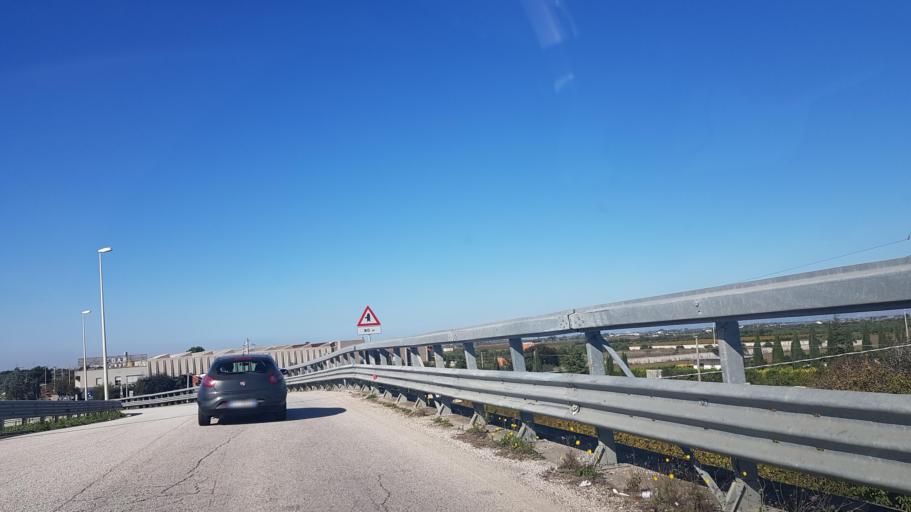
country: IT
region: Apulia
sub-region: Provincia di Foggia
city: Foggia
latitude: 41.4187
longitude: 15.6191
